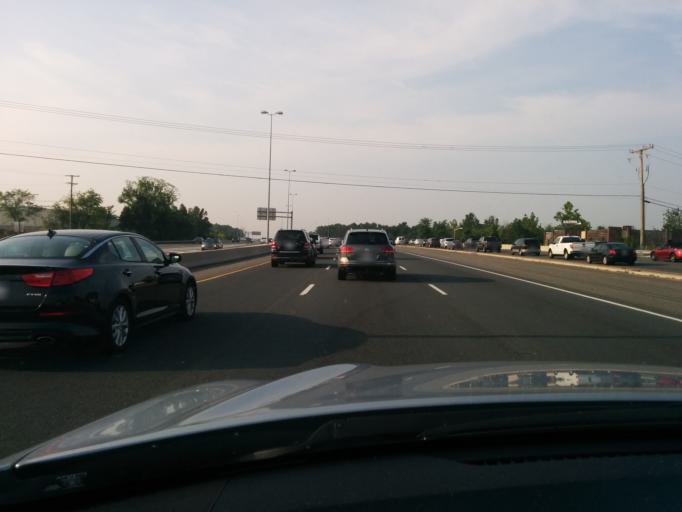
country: US
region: Virginia
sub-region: Loudoun County
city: Sterling
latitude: 39.0009
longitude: -77.4352
